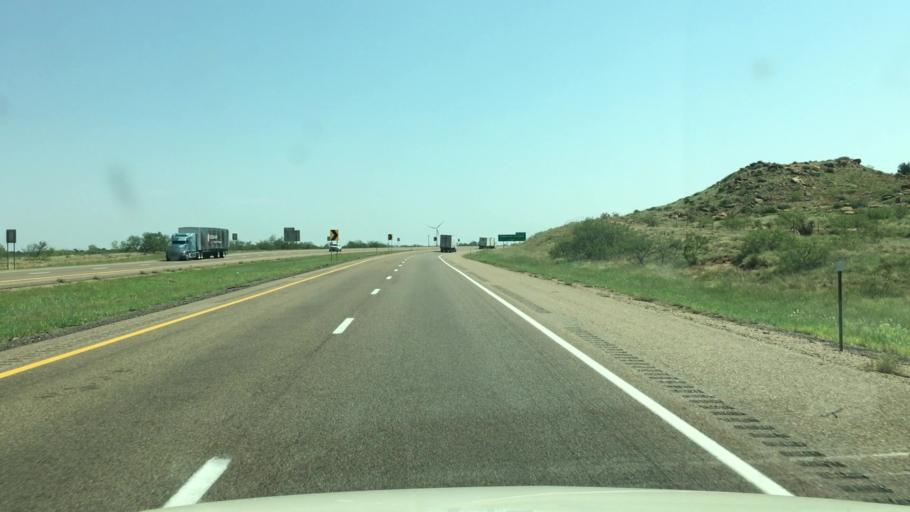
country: US
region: New Mexico
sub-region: Quay County
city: Tucumcari
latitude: 35.1549
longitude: -103.7691
